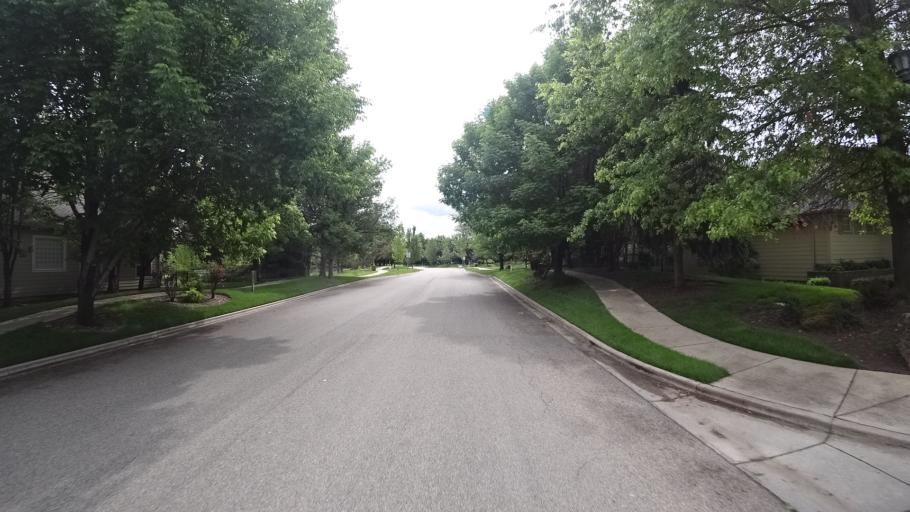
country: US
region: Idaho
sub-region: Ada County
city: Eagle
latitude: 43.6794
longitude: -116.3447
